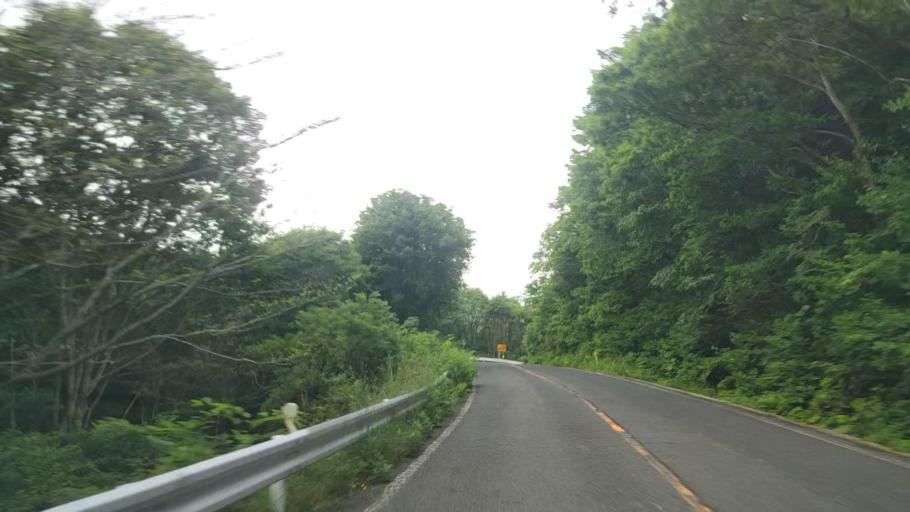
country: JP
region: Tottori
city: Yonago
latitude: 35.3327
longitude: 133.5699
